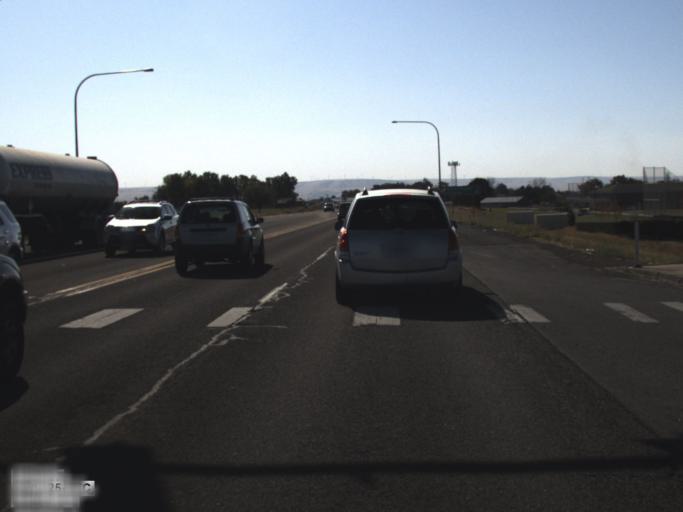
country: US
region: Washington
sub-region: Walla Walla County
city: College Place
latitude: 46.0318
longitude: -118.3809
